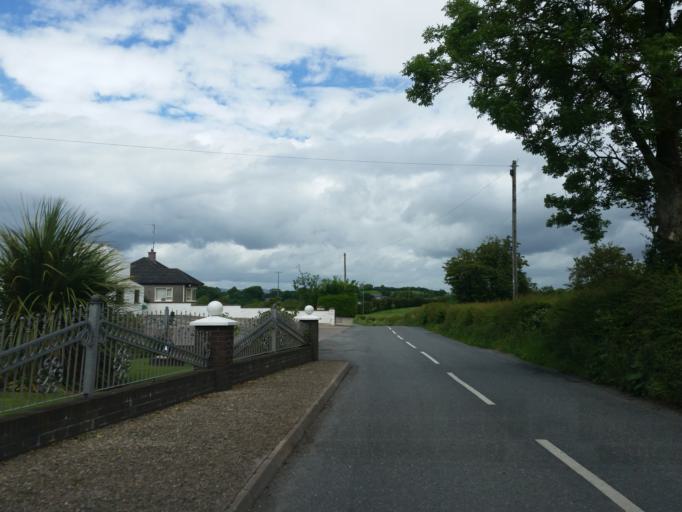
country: GB
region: Northern Ireland
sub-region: Omagh District
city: Omagh
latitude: 54.5468
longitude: -7.1164
